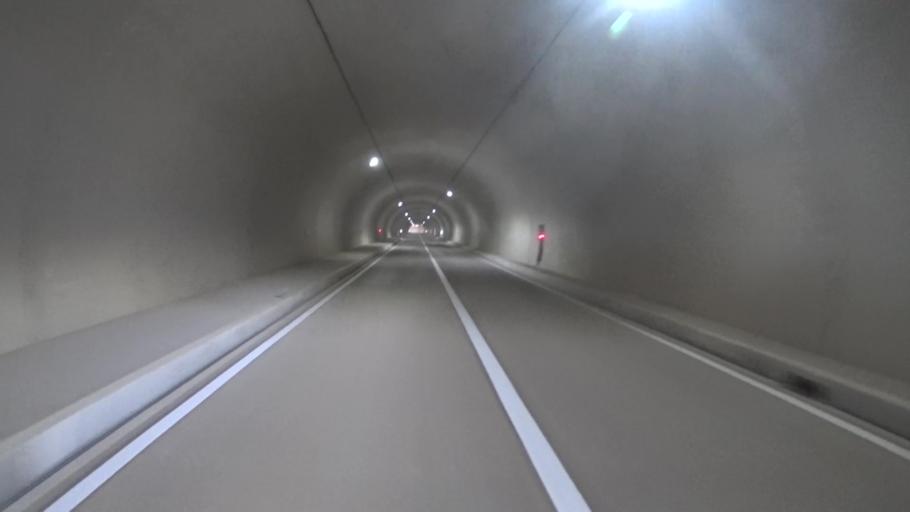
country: JP
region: Kyoto
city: Miyazu
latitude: 35.7430
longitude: 135.2559
